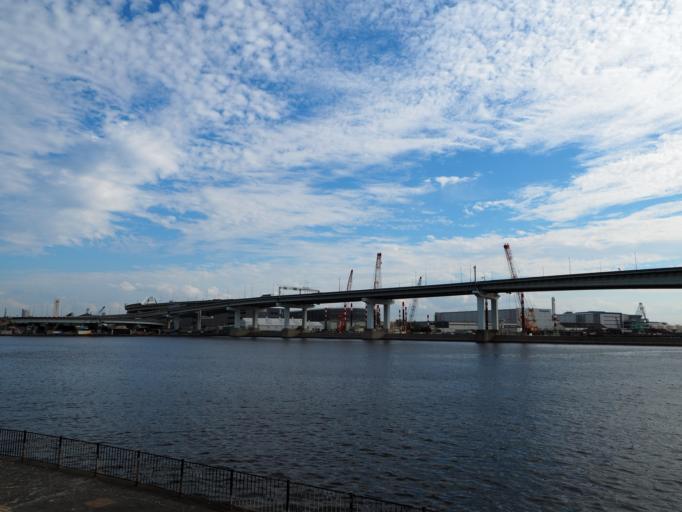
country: JP
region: Hyogo
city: Amagasaki
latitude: 34.7003
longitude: 135.3969
